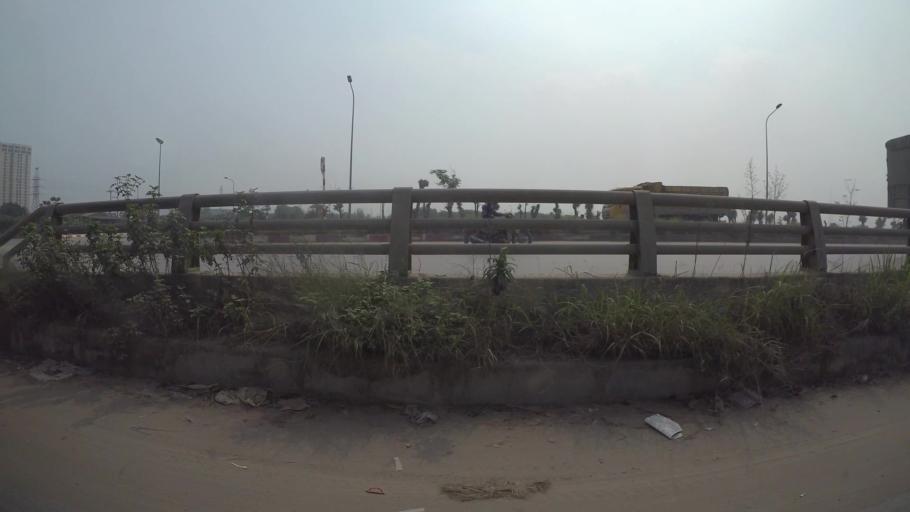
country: VN
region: Ha Noi
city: Cau Dien
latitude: 21.0113
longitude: 105.7469
